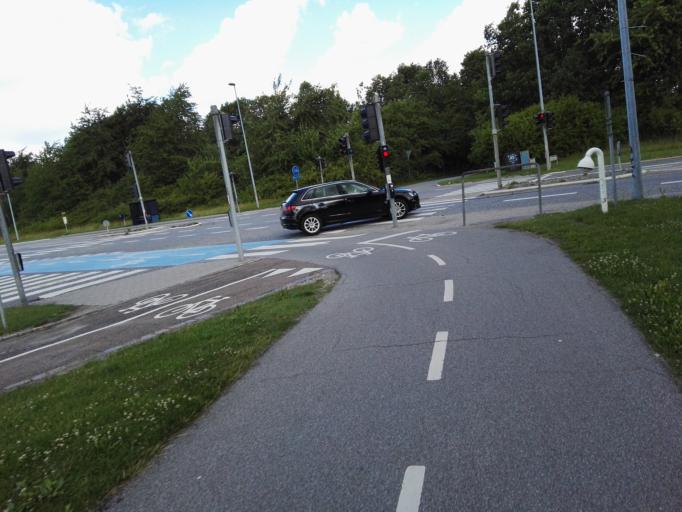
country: DK
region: Capital Region
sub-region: Ballerup Kommune
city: Ballerup
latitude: 55.7406
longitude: 12.3997
